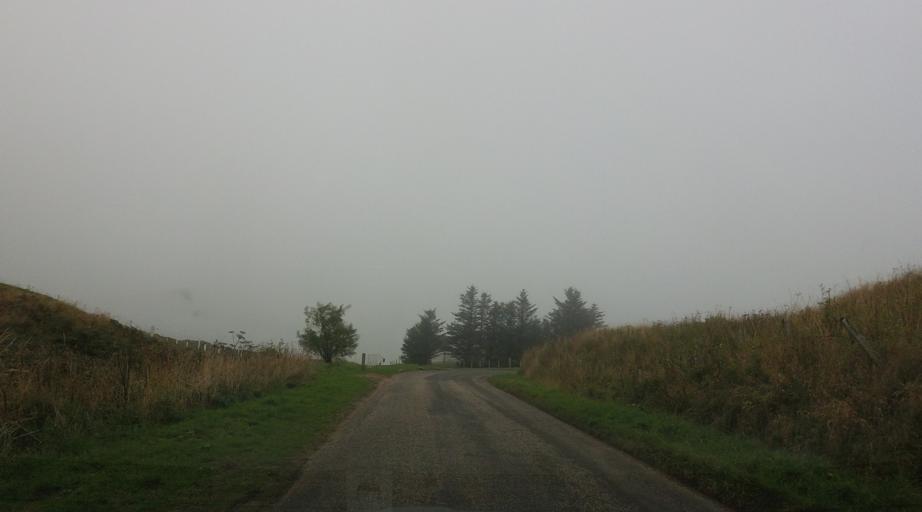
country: GB
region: Scotland
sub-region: Highland
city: Wick
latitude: 58.2995
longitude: -3.2889
